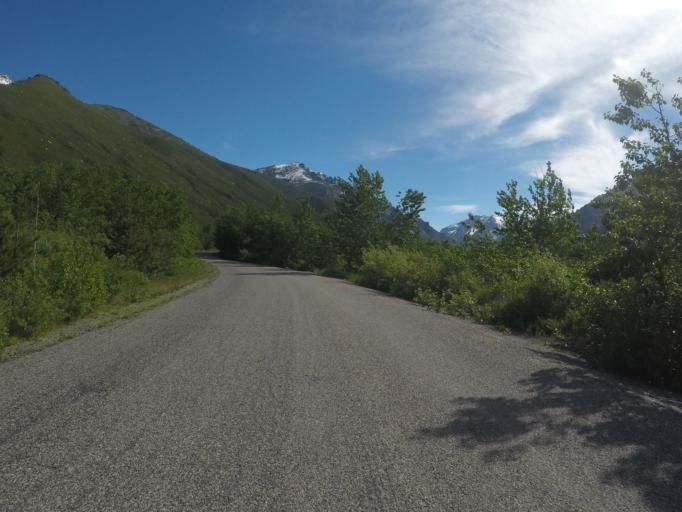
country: US
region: Montana
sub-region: Stillwater County
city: Absarokee
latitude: 45.2537
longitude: -109.5717
